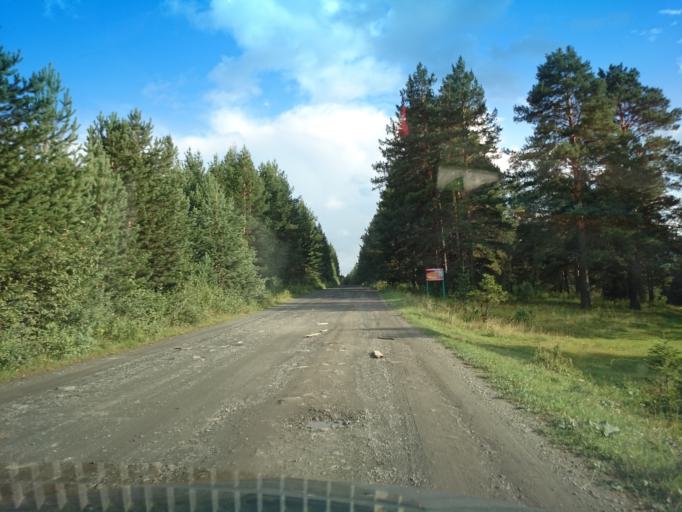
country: RU
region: Bashkortostan
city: Beloretsk
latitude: 54.0431
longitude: 58.3304
